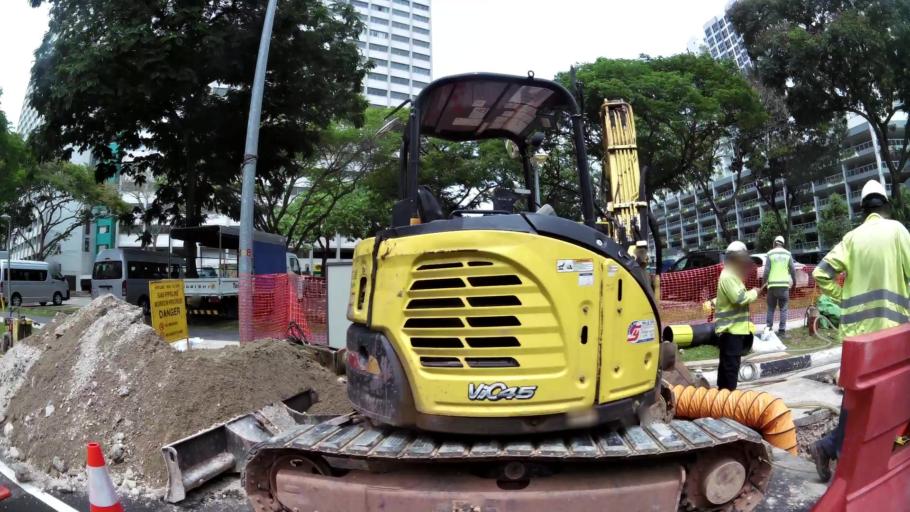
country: SG
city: Singapore
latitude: 1.3316
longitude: 103.7231
